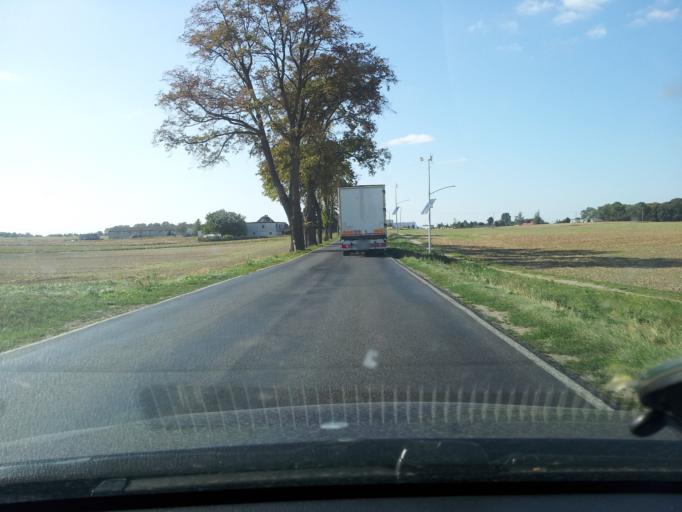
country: PL
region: Kujawsko-Pomorskie
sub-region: Powiat golubsko-dobrzynski
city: Kowalewo Pomorskie
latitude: 53.1584
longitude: 18.9294
